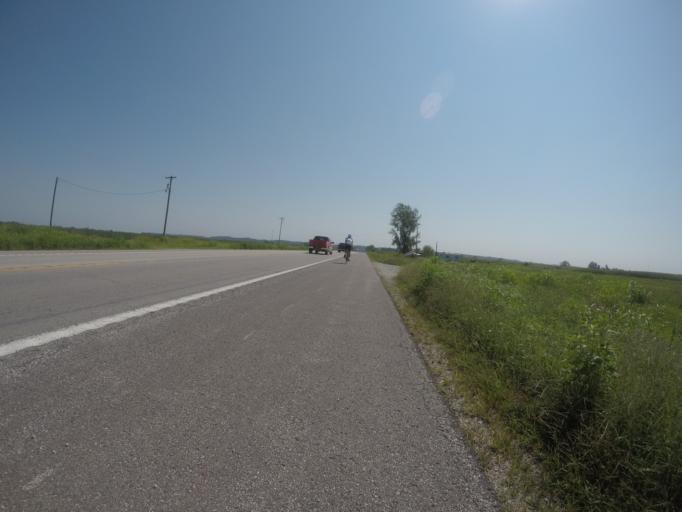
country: US
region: Kansas
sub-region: Atchison County
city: Atchison
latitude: 39.5569
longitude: -95.0928
